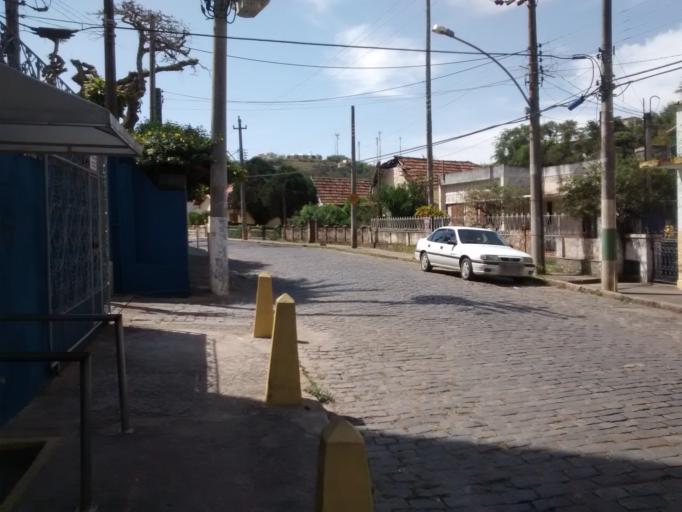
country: BR
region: Rio de Janeiro
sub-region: Miguel Pereira
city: Miguel Pereira
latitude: -22.4578
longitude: -43.4686
